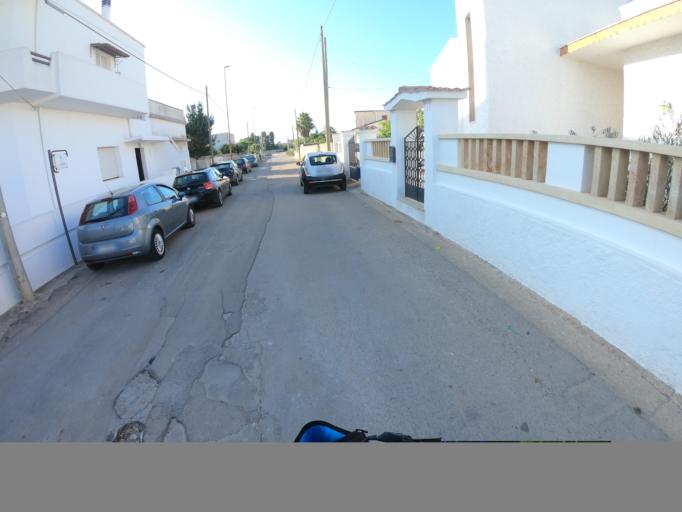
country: IT
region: Apulia
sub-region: Provincia di Lecce
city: Castrignano del Capo
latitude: 39.8353
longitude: 18.3563
